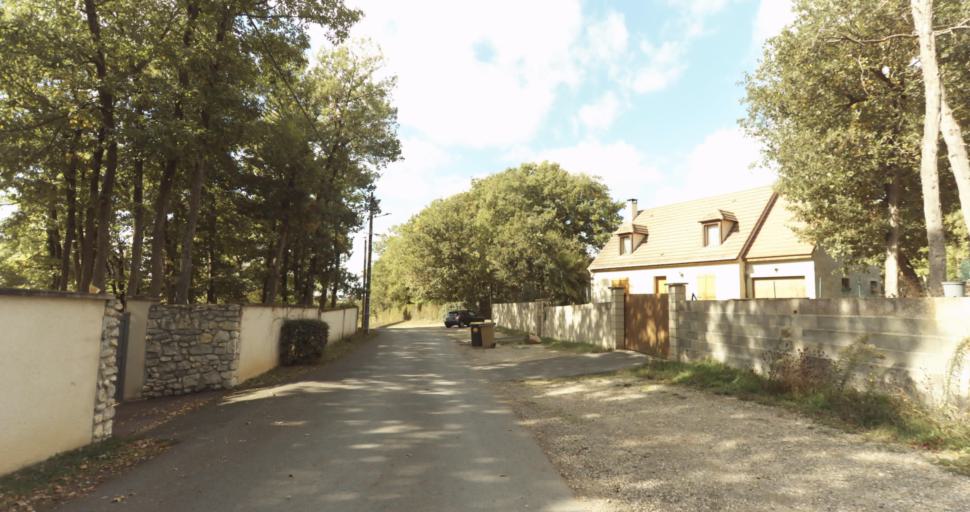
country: FR
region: Centre
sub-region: Departement d'Eure-et-Loir
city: Garnay
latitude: 48.7208
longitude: 1.3404
